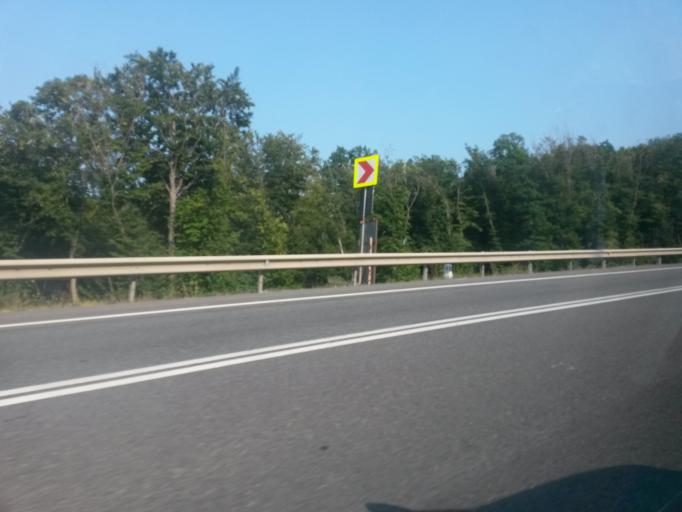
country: RO
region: Cluj
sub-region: Comuna Feleacu
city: Gheorghieni
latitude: 46.7176
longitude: 23.6613
